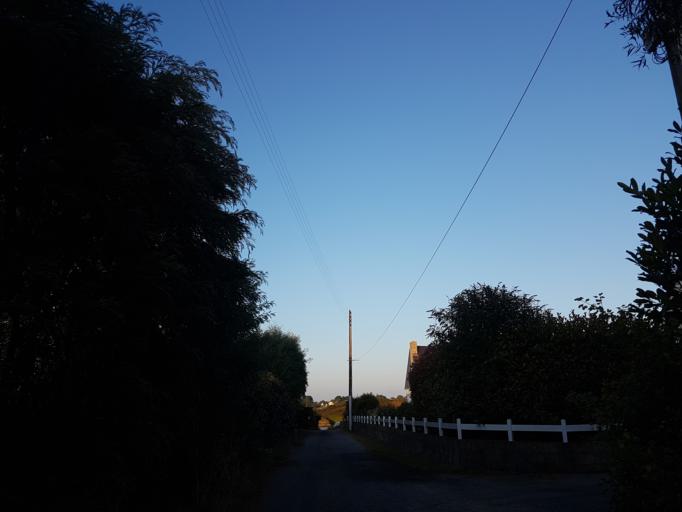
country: FR
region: Brittany
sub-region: Departement du Morbihan
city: Etel
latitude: 47.6816
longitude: -3.2019
